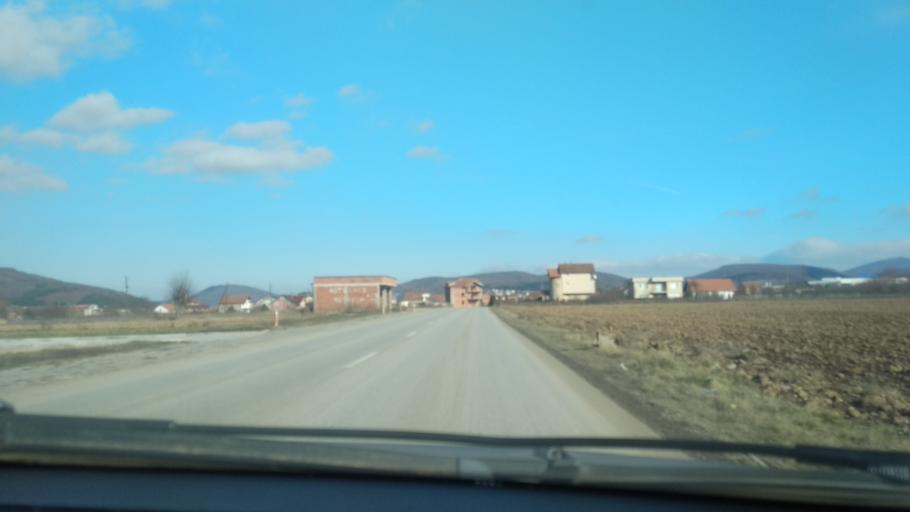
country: XK
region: Pristina
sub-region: Komuna e Obiliqit
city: Obiliq
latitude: 42.7412
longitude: 21.1241
